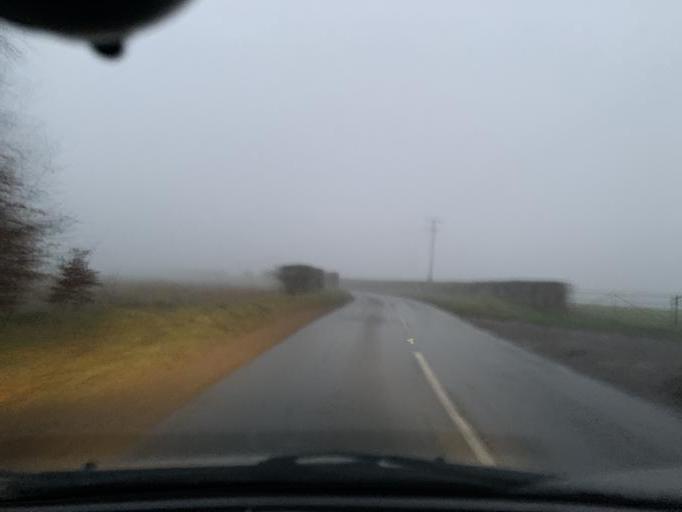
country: GB
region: England
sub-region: Wiltshire
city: Shrewton
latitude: 51.2015
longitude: -1.8841
